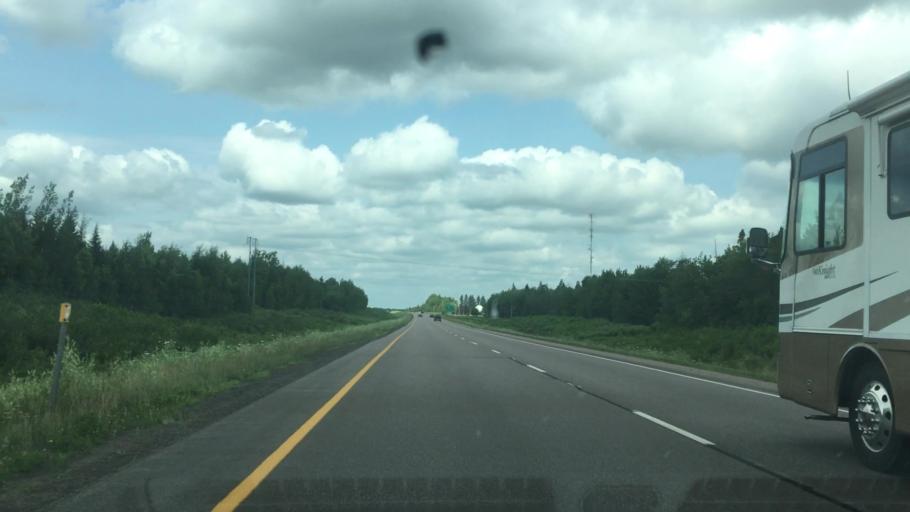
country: CA
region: New Brunswick
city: Dieppe
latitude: 46.0791
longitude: -64.5931
